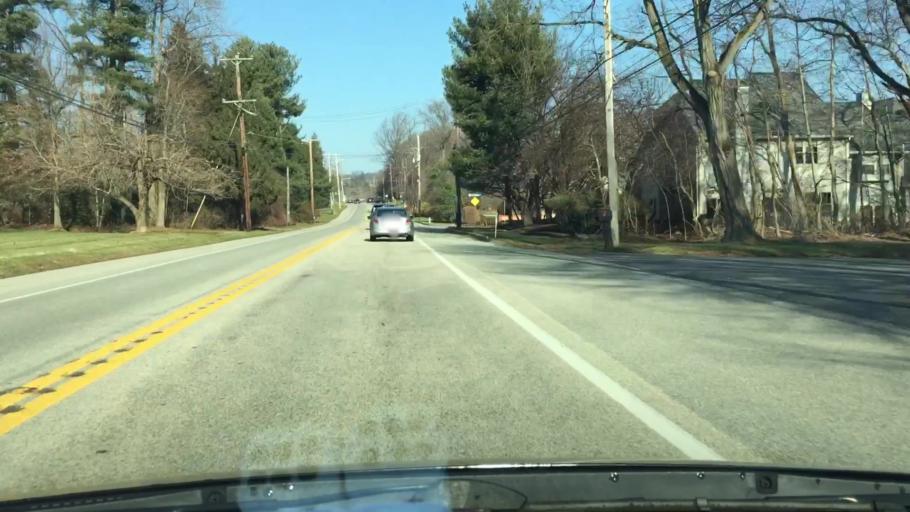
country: US
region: Pennsylvania
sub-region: Delaware County
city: Media
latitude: 39.9580
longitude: -75.3935
